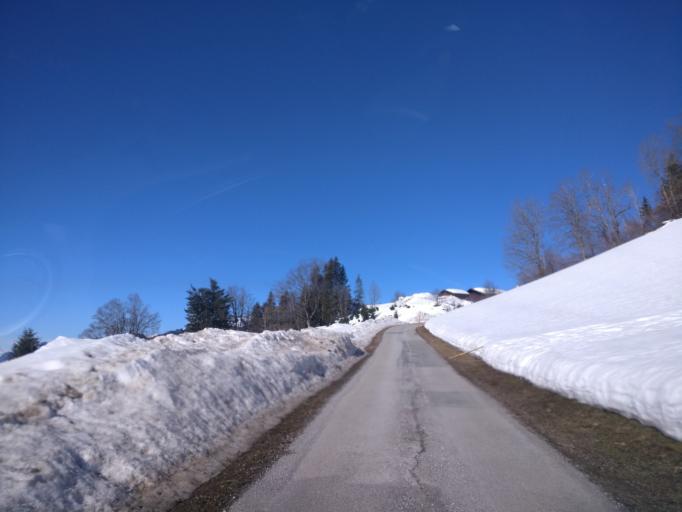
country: AT
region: Salzburg
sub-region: Politischer Bezirk Sankt Johann im Pongau
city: Sankt Johann im Pongau
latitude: 47.3373
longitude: 13.2269
